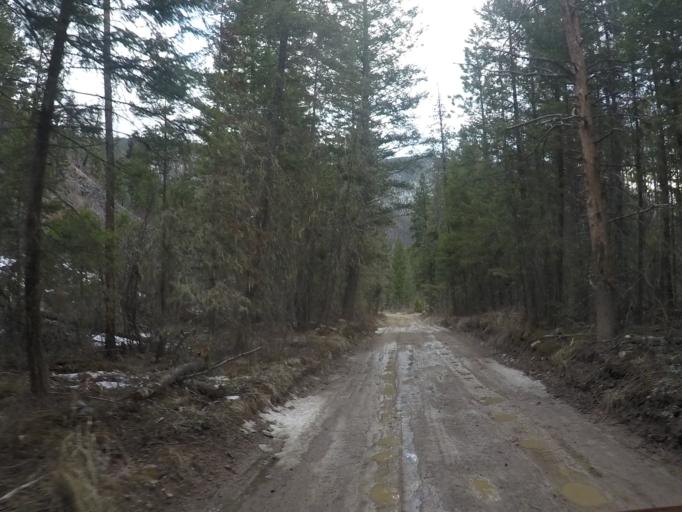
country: US
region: Montana
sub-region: Missoula County
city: Clinton
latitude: 46.5672
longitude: -113.6995
